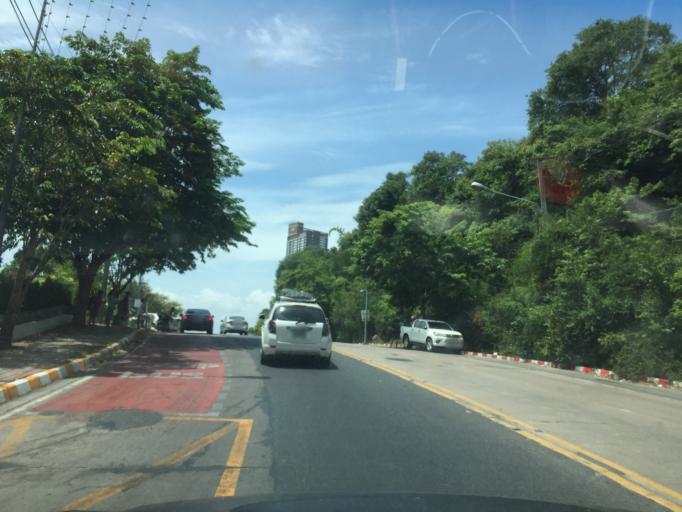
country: TH
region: Chon Buri
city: Phatthaya
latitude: 12.9240
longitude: 100.8667
